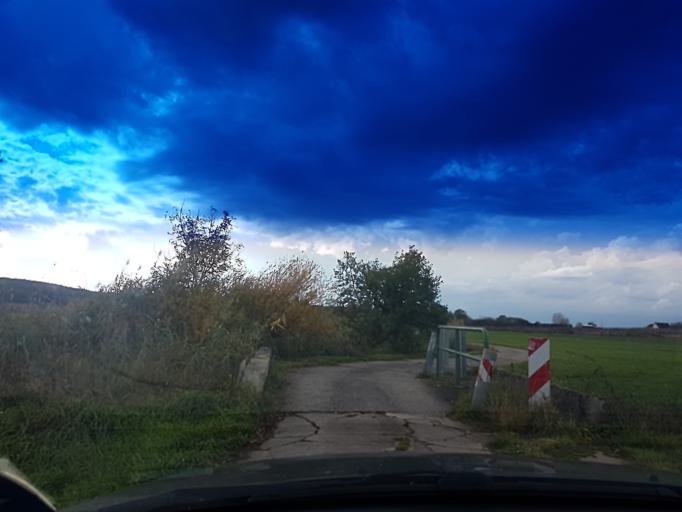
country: DE
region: Bavaria
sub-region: Regierungsbezirk Mittelfranken
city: Muhlhausen
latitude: 49.7498
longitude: 10.7599
